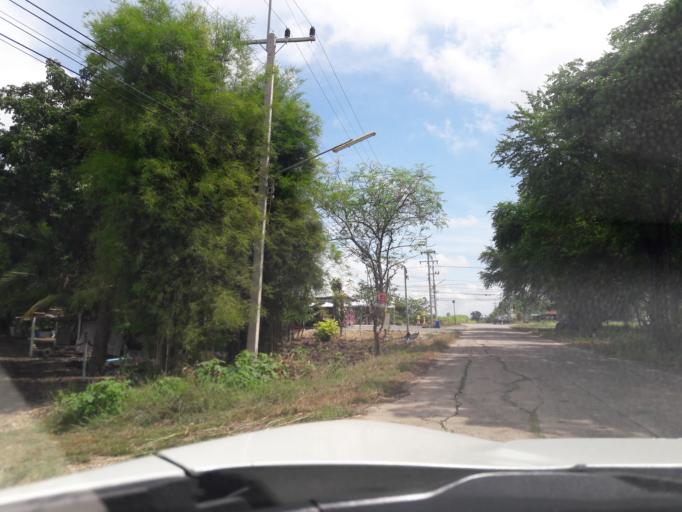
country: TH
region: Lop Buri
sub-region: Amphoe Tha Luang
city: Tha Luang
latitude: 15.0740
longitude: 101.1201
